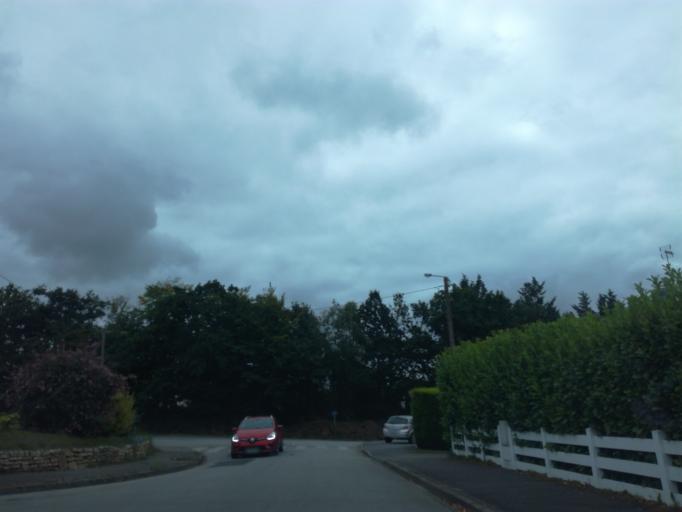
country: FR
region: Brittany
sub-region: Departement du Morbihan
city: Pontivy
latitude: 48.0556
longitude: -2.9575
